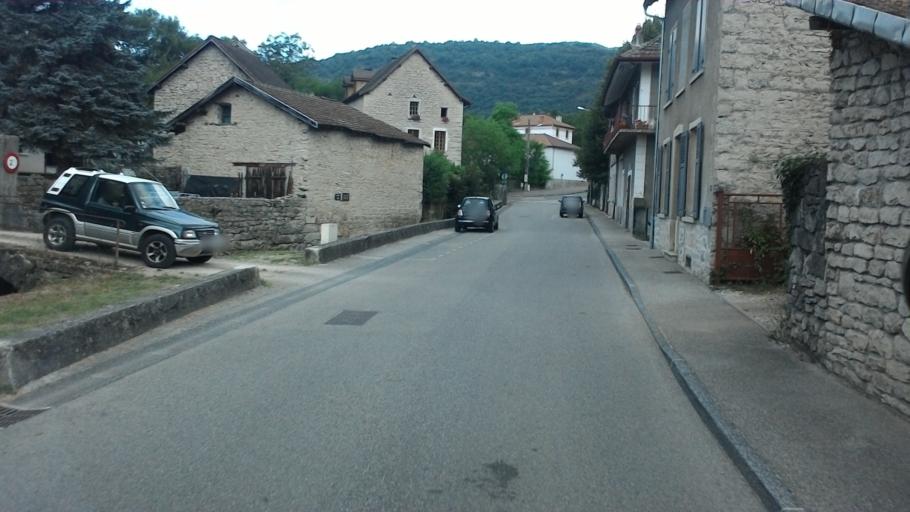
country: FR
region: Rhone-Alpes
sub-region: Departement de l'Ain
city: Villebois
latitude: 45.8503
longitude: 5.4341
